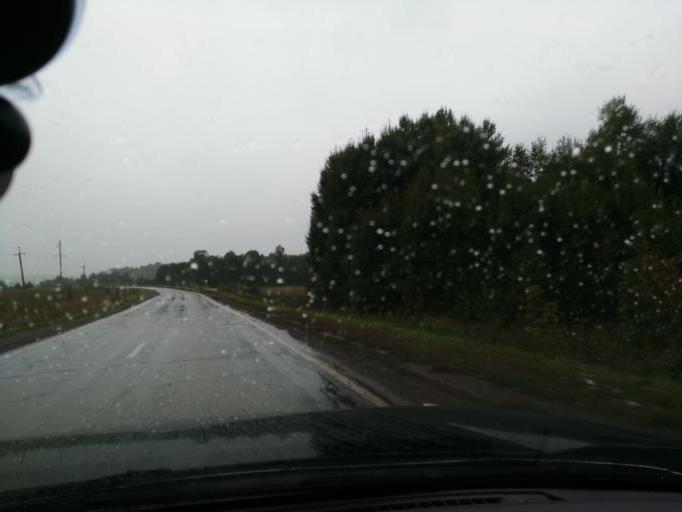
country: RU
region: Perm
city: Barda
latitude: 56.9430
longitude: 55.6396
